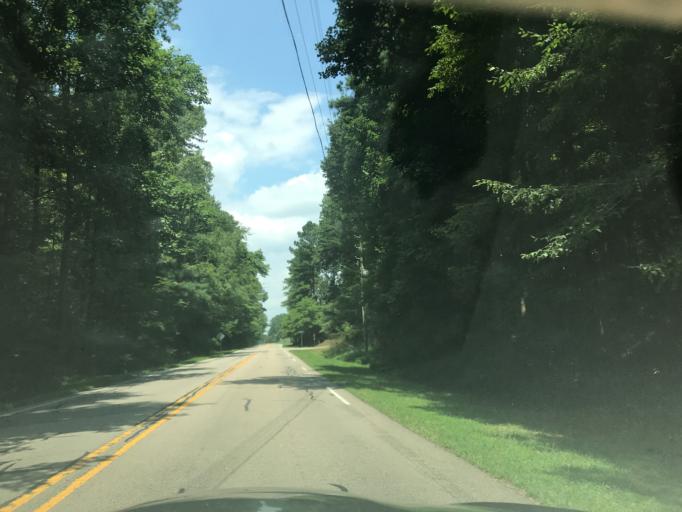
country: US
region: North Carolina
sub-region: Wake County
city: Cary
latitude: 35.8360
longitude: -78.7218
